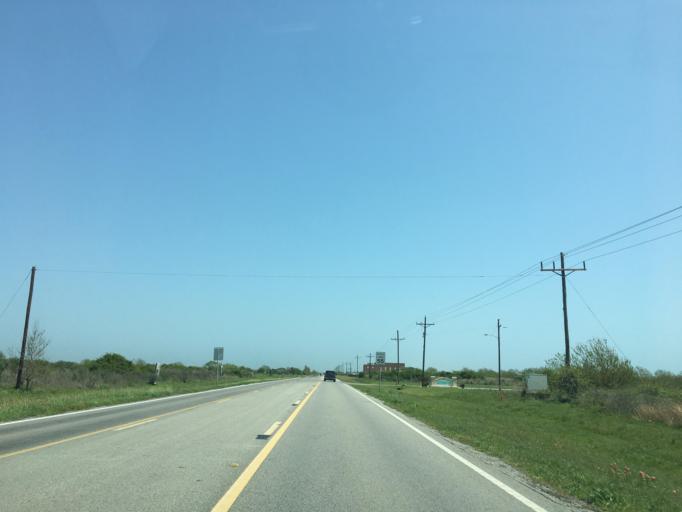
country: US
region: Texas
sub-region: Galveston County
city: Bolivar Peninsula
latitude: 29.4250
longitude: -94.6956
